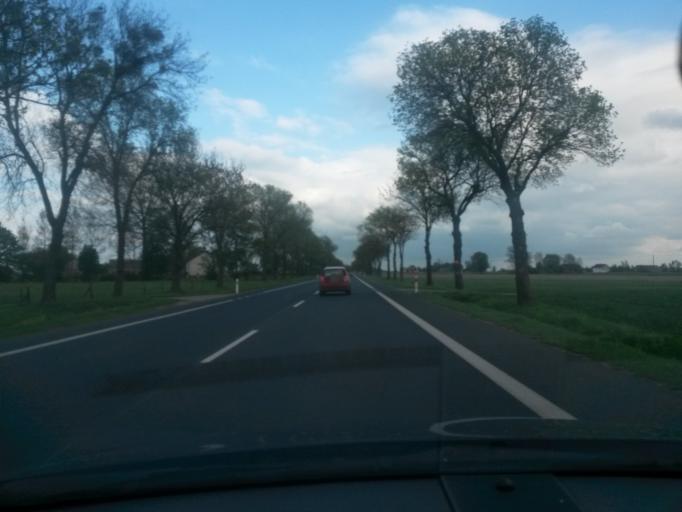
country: PL
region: Masovian Voivodeship
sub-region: Powiat plocki
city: Drobin
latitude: 52.7703
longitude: 19.9287
